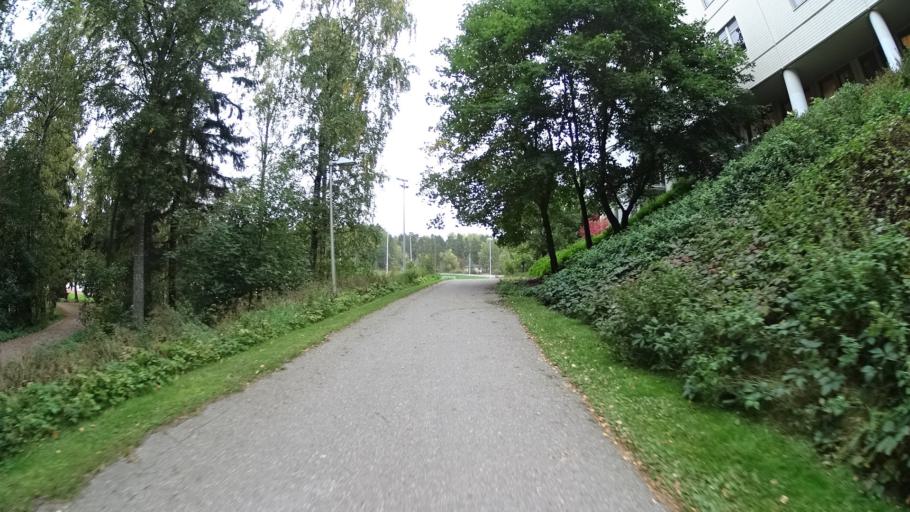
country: FI
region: Uusimaa
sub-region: Helsinki
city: Vantaa
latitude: 60.2073
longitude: 25.0352
